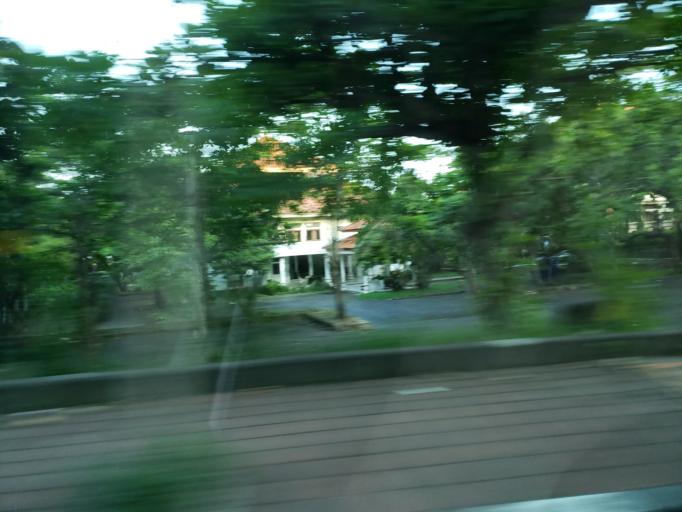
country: ID
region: Bali
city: Jimbaran
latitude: -8.7955
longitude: 115.1757
